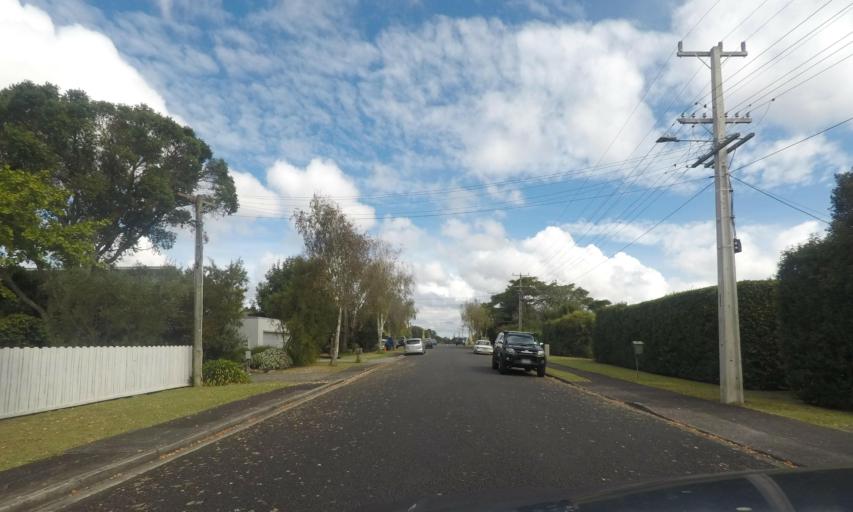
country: NZ
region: Auckland
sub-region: Auckland
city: Rosebank
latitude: -36.7805
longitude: 174.6447
